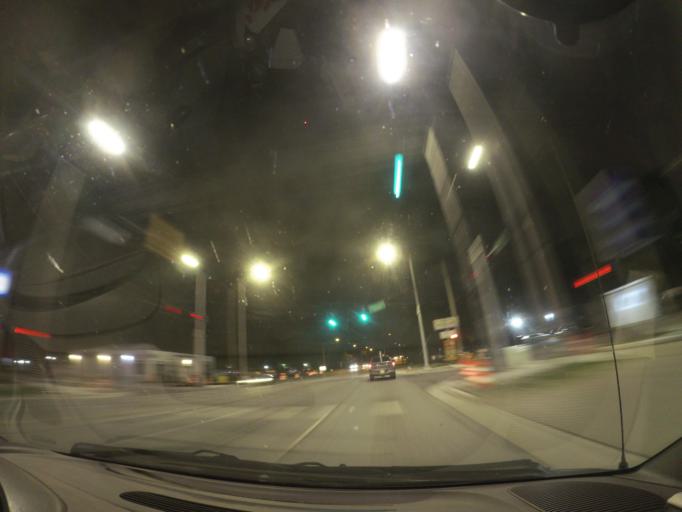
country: US
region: Illinois
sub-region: Cook County
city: Markham
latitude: 41.6008
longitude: -87.7040
